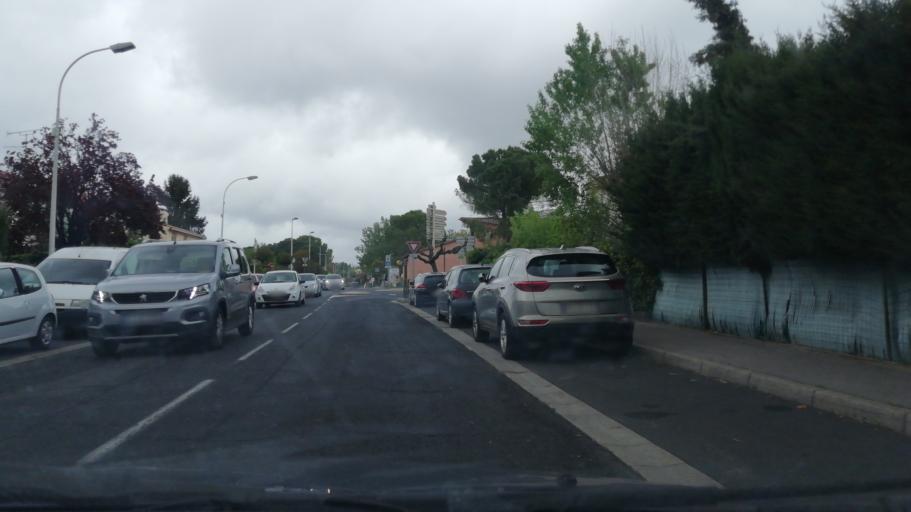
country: FR
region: Languedoc-Roussillon
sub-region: Departement de l'Herault
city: Saint-Gely-du-Fesc
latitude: 43.6919
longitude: 3.8073
